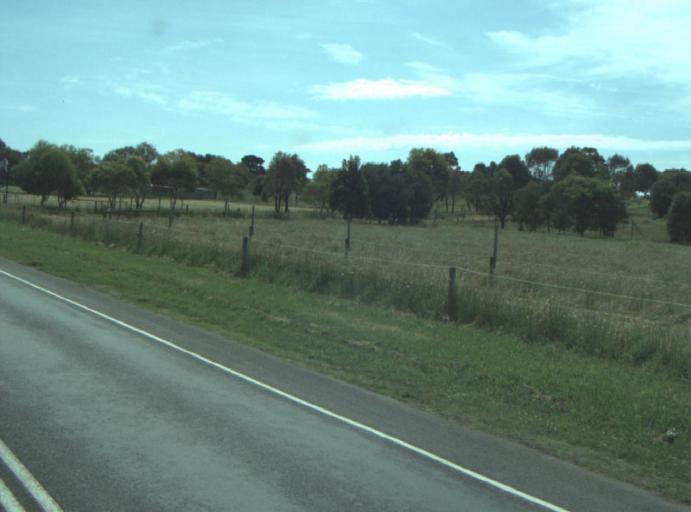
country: AU
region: Victoria
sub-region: Greater Geelong
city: Clifton Springs
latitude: -38.1572
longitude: 144.5864
